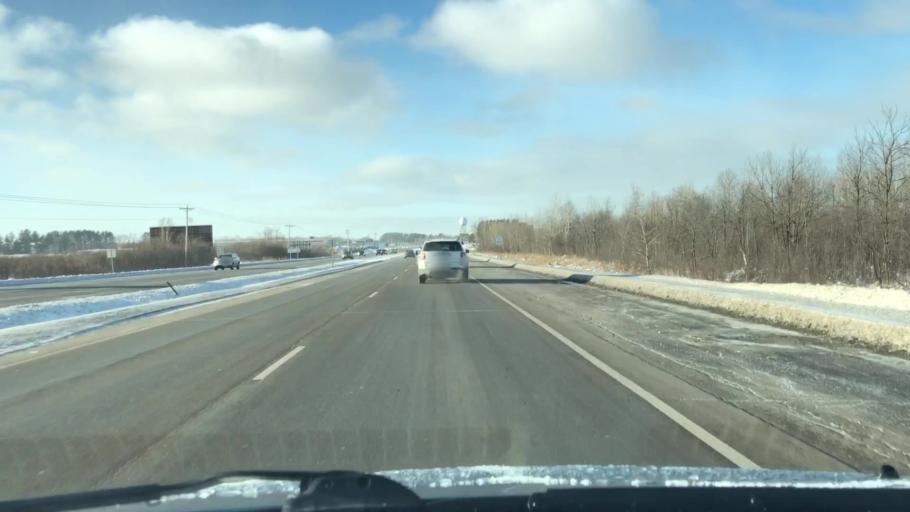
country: US
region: Minnesota
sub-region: Saint Louis County
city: Hermantown
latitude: 46.8292
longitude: -92.1981
